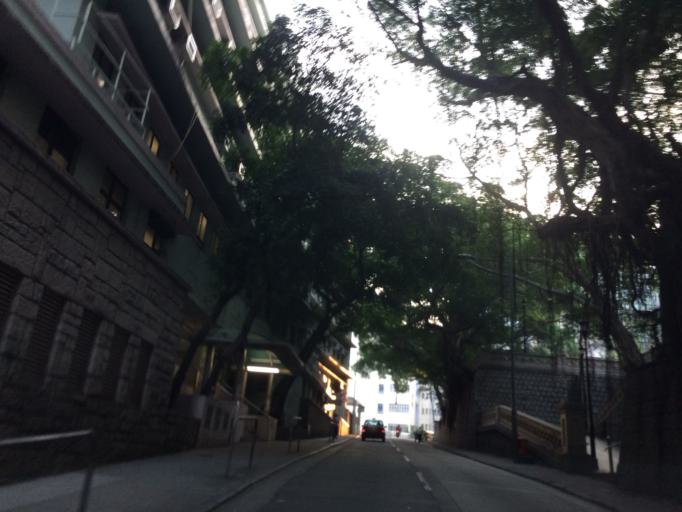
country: HK
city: Hong Kong
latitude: 22.2860
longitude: 114.1442
